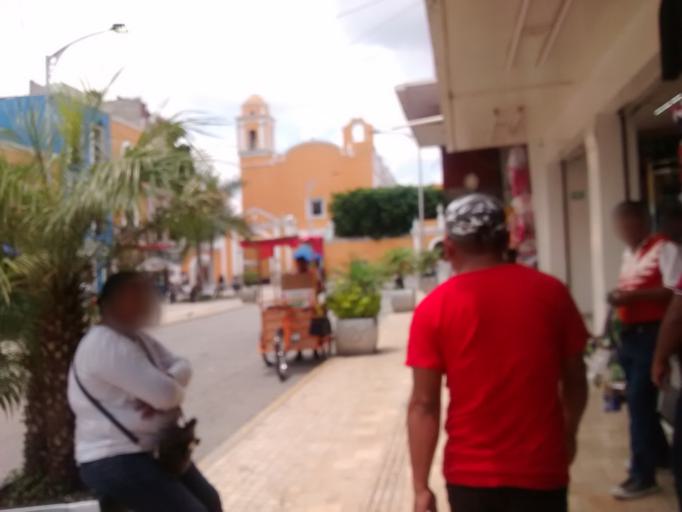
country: MX
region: Puebla
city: Tehuacan
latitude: 18.4620
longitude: -97.3912
